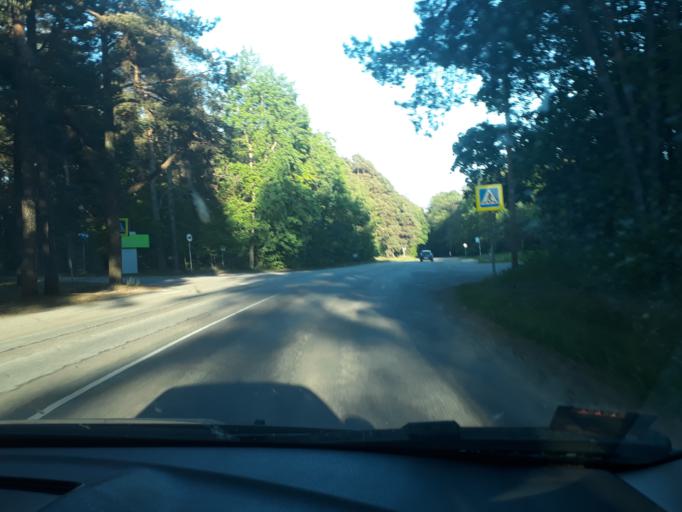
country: EE
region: Paernumaa
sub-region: Paernu linn
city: Parnu
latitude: 58.3856
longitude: 24.5350
